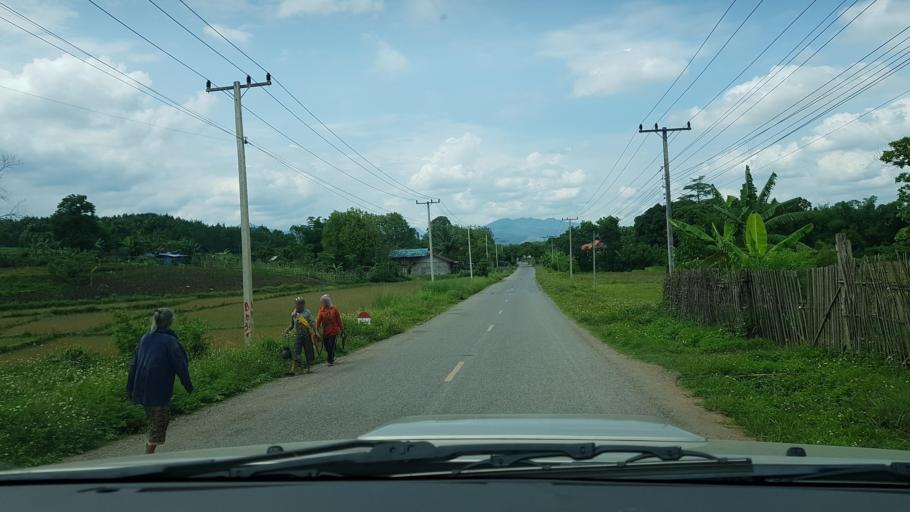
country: LA
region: Loungnamtha
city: Muang Nale
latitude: 20.1117
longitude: 101.4183
